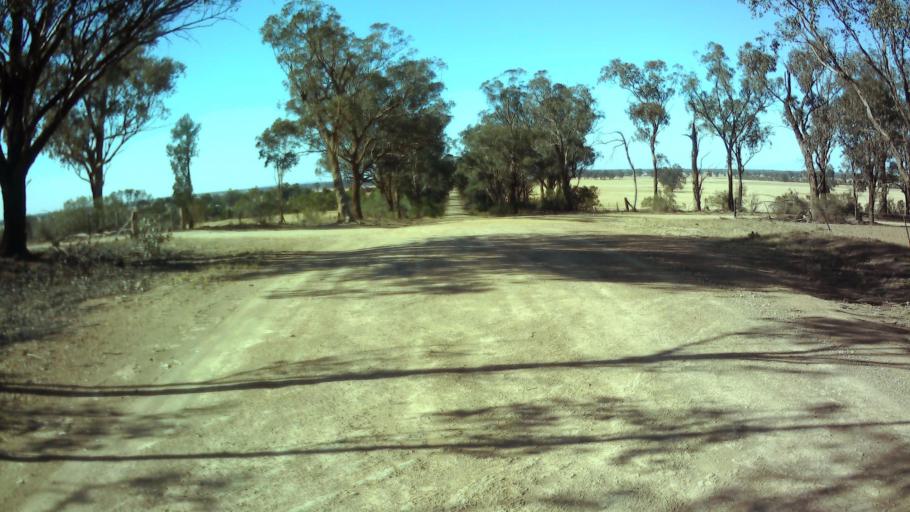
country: AU
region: New South Wales
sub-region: Weddin
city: Grenfell
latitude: -33.9012
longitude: 147.8784
